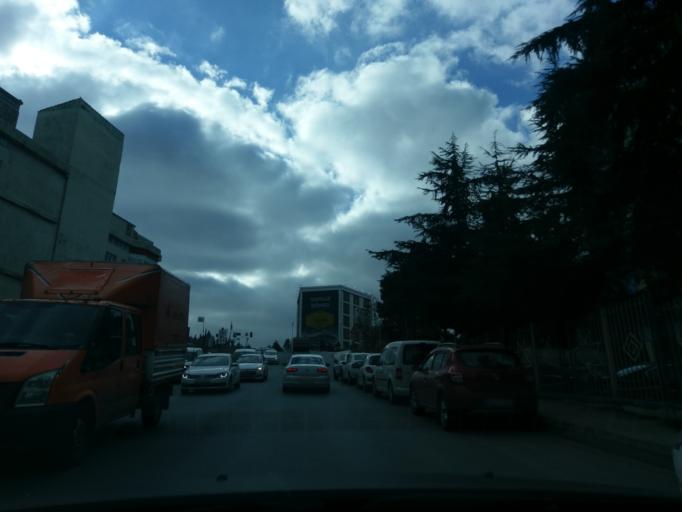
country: TR
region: Istanbul
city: Basaksehir
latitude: 41.0899
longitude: 28.8022
